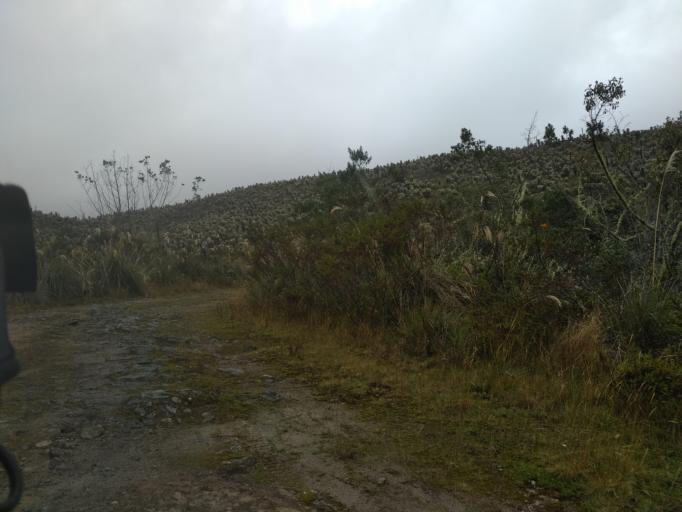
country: EC
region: Carchi
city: San Gabriel
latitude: 0.7055
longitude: -77.8301
